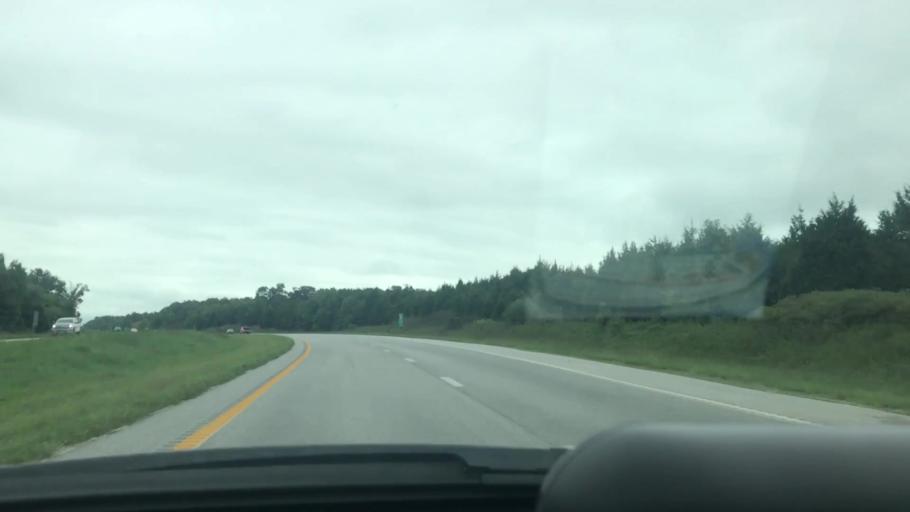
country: US
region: Missouri
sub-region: Greene County
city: Fair Grove
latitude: 37.3190
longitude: -93.1687
